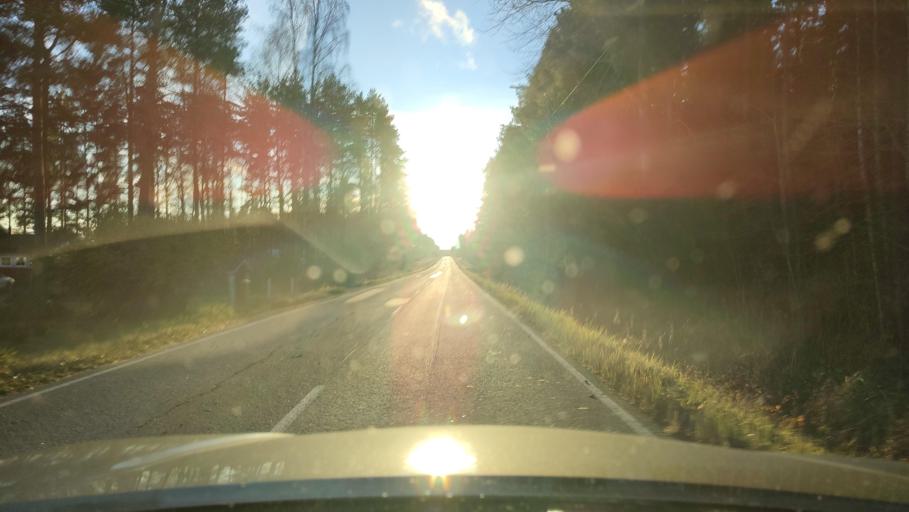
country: FI
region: Ostrobothnia
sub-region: Vaasa
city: Malax
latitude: 62.6985
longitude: 21.5767
